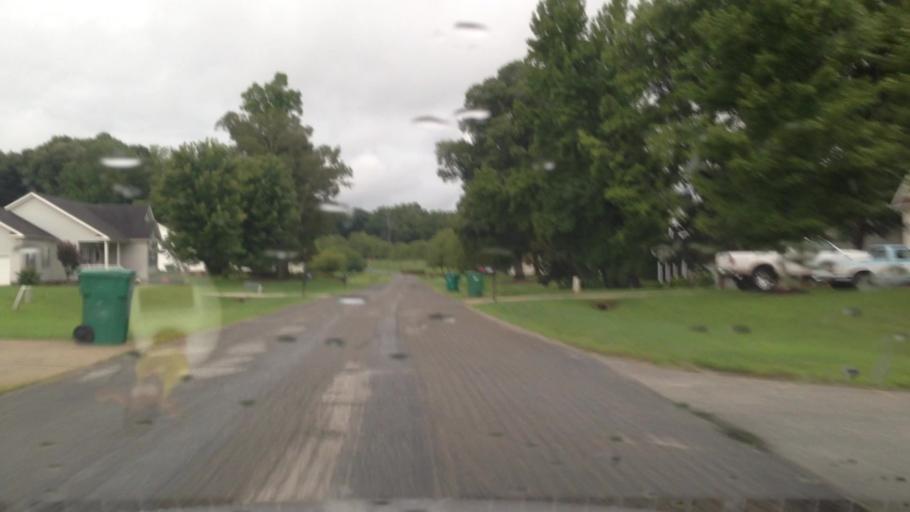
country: US
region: North Carolina
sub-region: Rockingham County
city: Reidsville
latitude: 36.2642
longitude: -79.7200
